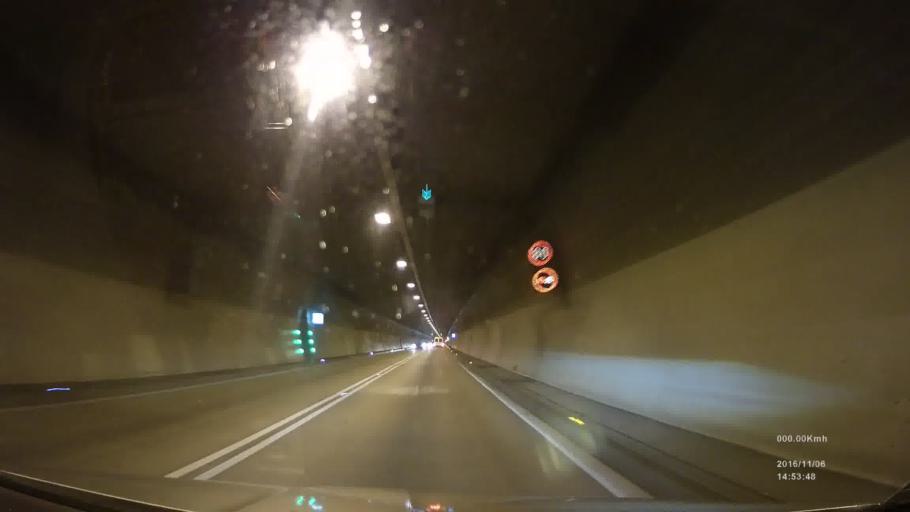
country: SK
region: Kosicky
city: Krompachy
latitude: 49.0058
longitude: 20.8657
